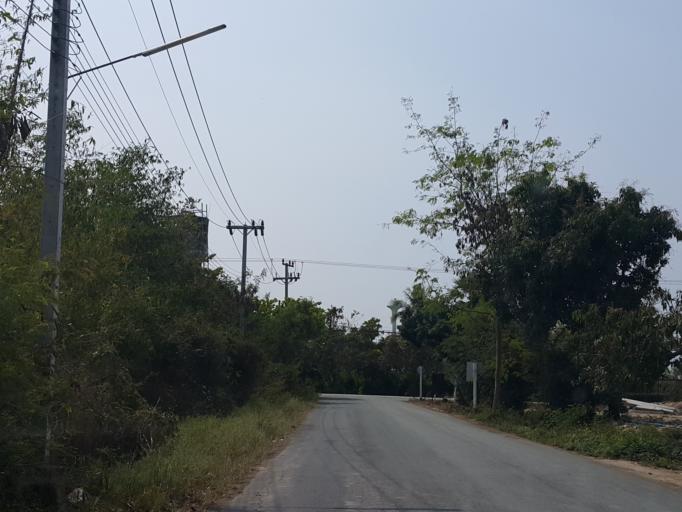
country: TH
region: Lamphun
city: Ban Thi
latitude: 18.6659
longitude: 99.0984
